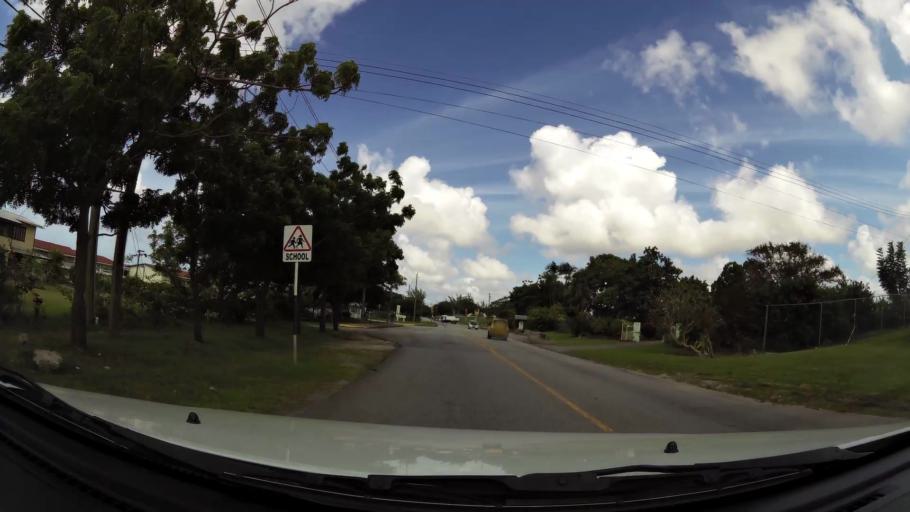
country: BB
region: Saint James
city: Holetown
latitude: 13.1451
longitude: -59.6227
